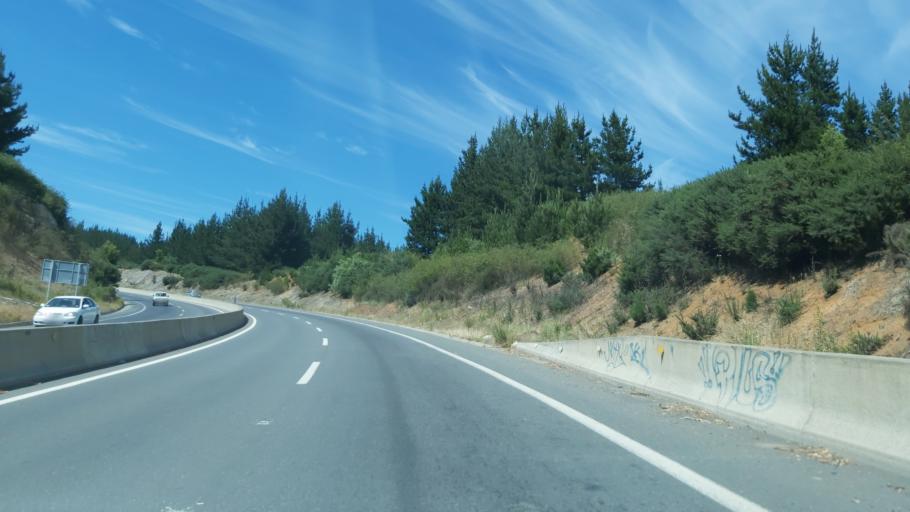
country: CL
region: Biobio
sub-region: Provincia de Concepcion
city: Lota
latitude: -37.0767
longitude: -73.1380
